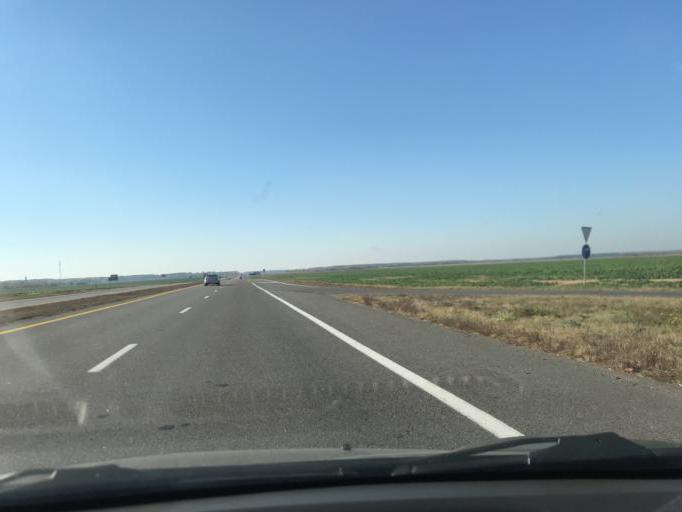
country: BY
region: Gomel
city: Horad Rechytsa
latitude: 52.2915
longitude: 30.4629
